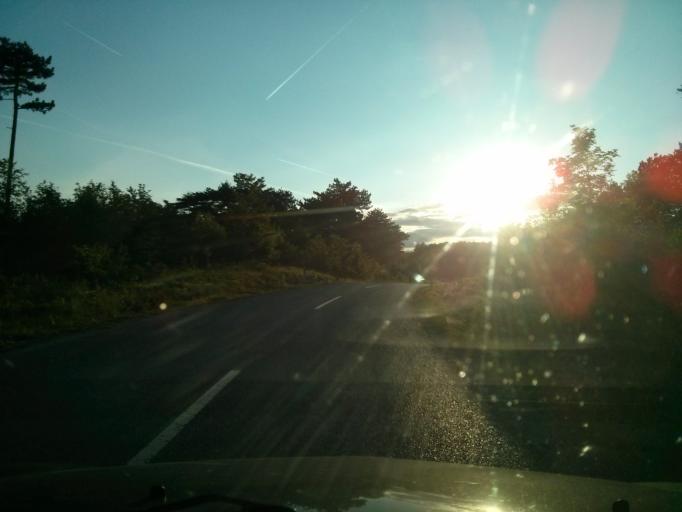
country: AT
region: Lower Austria
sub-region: Politischer Bezirk Baden
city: Hirtenberg
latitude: 47.9112
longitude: 16.1507
